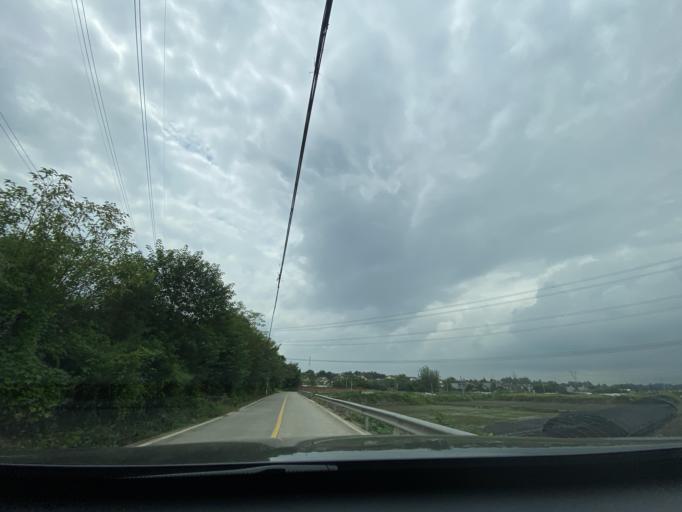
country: CN
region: Sichuan
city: Wujin
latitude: 30.3739
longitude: 103.9697
